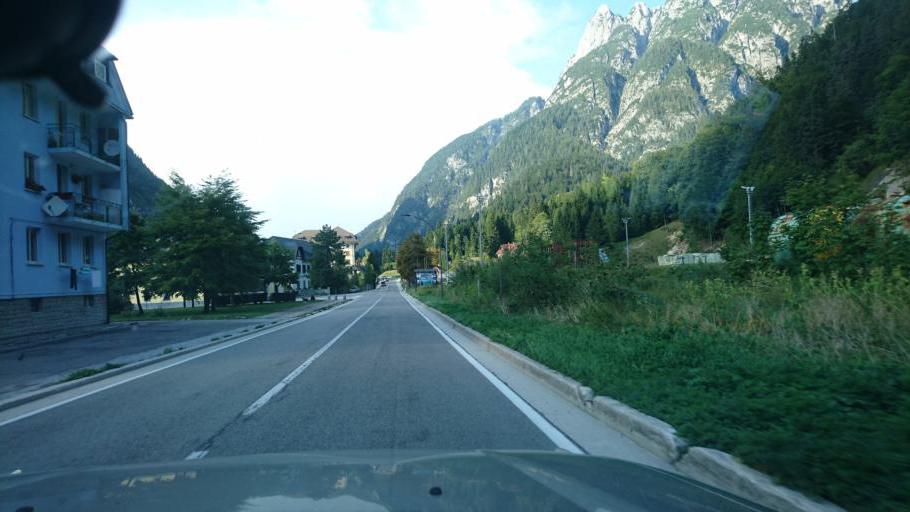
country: IT
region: Friuli Venezia Giulia
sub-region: Provincia di Udine
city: Tarvisio
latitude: 46.4416
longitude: 13.5725
